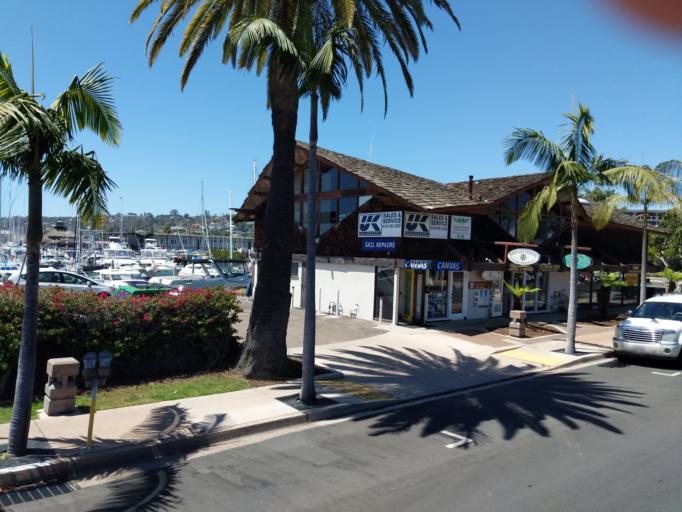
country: US
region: California
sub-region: San Diego County
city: Coronado
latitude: 32.7201
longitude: -117.2267
